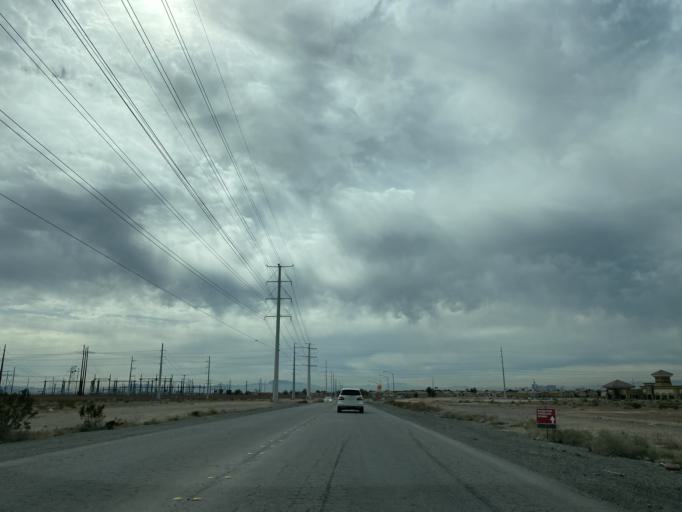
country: US
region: Nevada
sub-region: Clark County
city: Nellis Air Force Base
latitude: 36.2798
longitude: -115.0987
